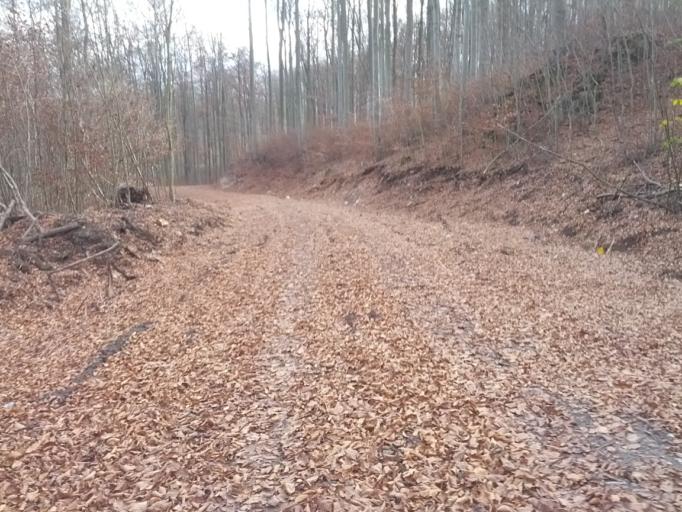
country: DE
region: Thuringia
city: Krauthausen
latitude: 50.9764
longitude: 10.2350
